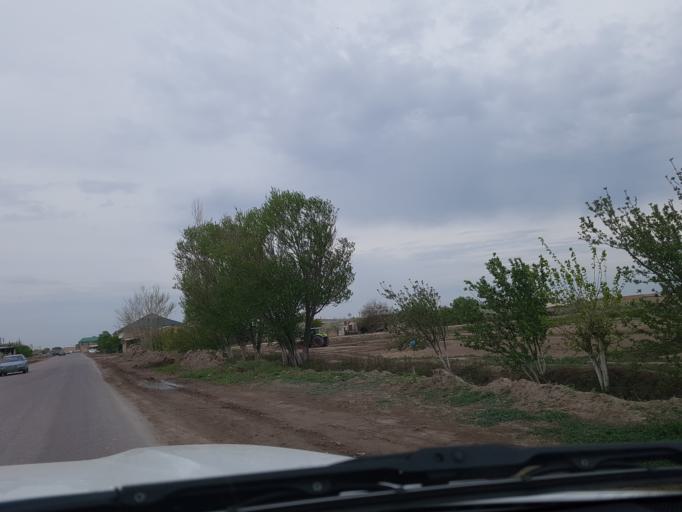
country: TM
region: Lebap
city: Turkmenabat
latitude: 39.0655
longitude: 63.5503
